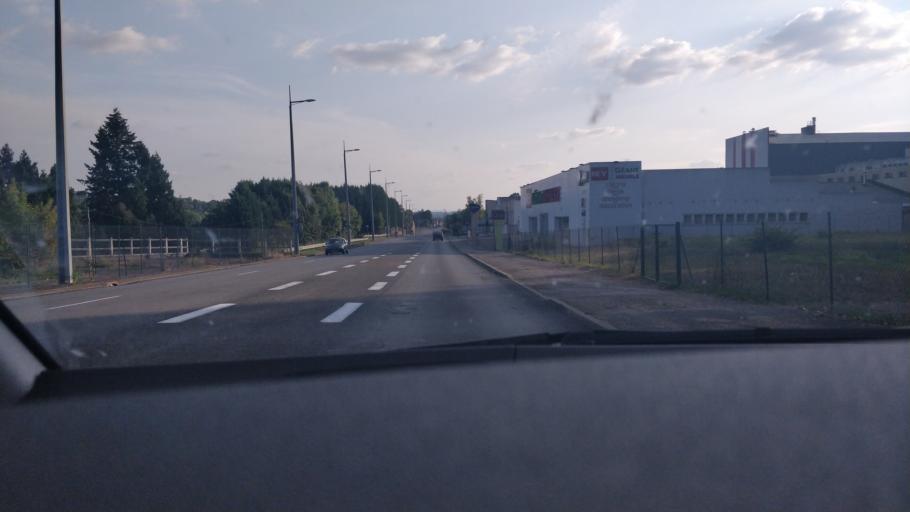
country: FR
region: Limousin
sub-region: Departement de la Haute-Vienne
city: Le Palais-sur-Vienne
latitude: 45.8464
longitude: 1.2917
